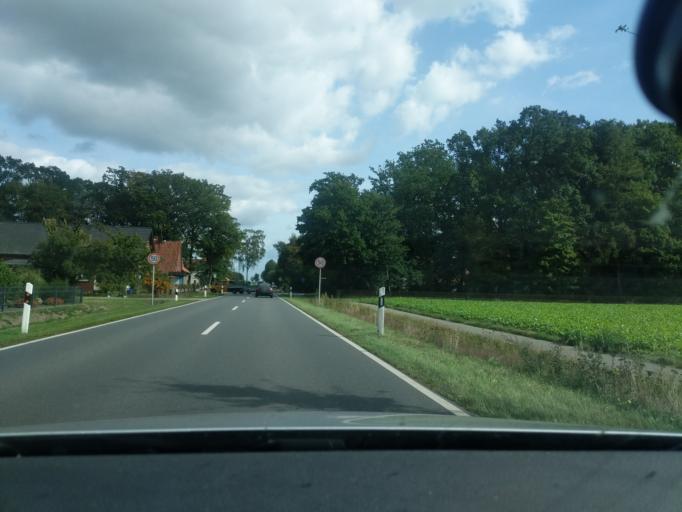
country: DE
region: Lower Saxony
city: Maasen
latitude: 52.6923
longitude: 8.8819
